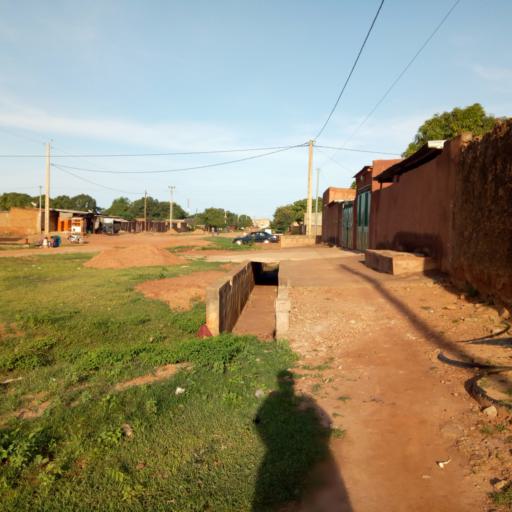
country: ML
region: Sikasso
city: Koutiala
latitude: 12.4093
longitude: -5.4509
